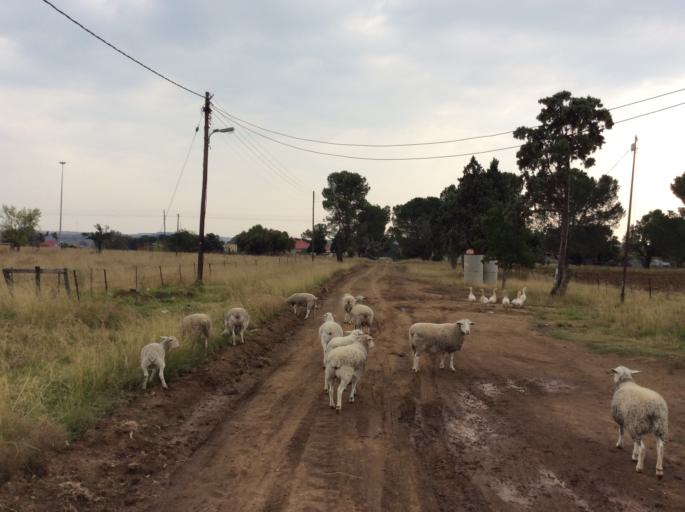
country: LS
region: Mafeteng
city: Mafeteng
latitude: -29.9896
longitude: 27.0167
